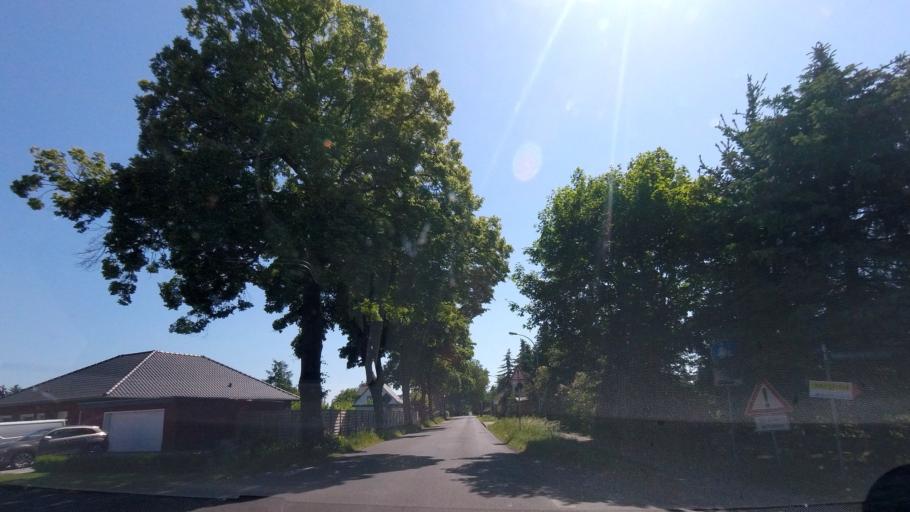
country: DE
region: Brandenburg
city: Gross Kreutz
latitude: 52.4036
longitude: 12.7152
